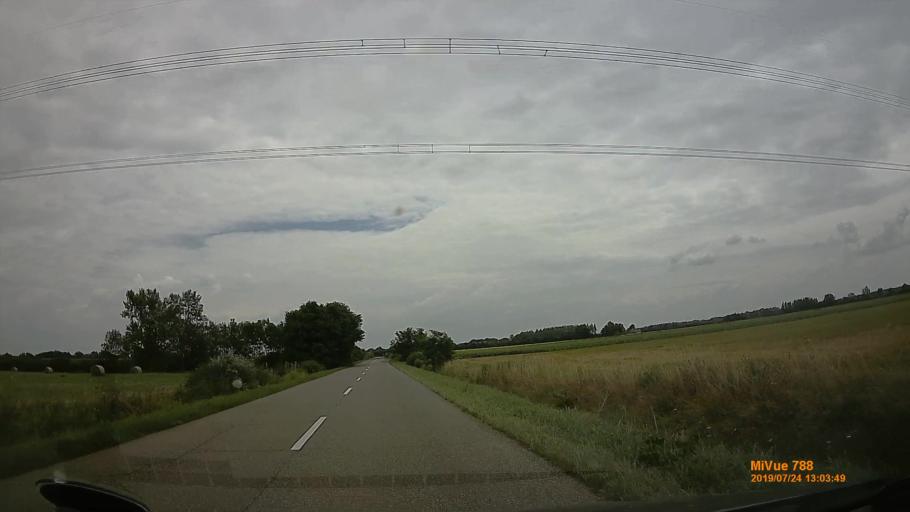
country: HU
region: Szabolcs-Szatmar-Bereg
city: Aranyosapati
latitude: 48.2077
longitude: 22.3023
